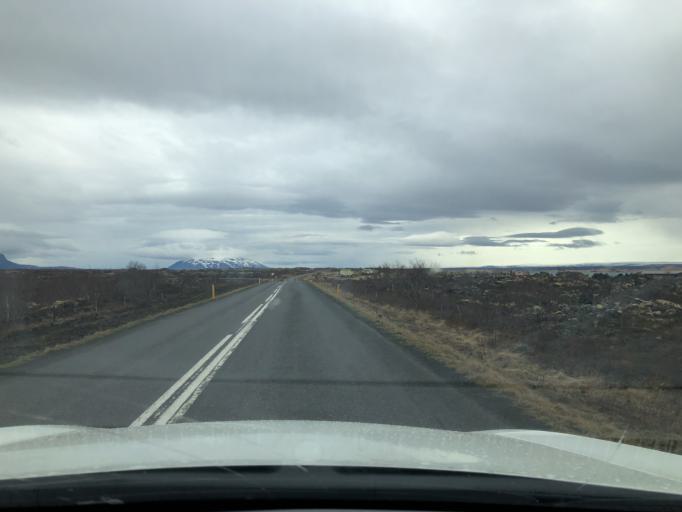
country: IS
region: Northeast
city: Laugar
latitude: 65.6038
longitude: -16.9238
